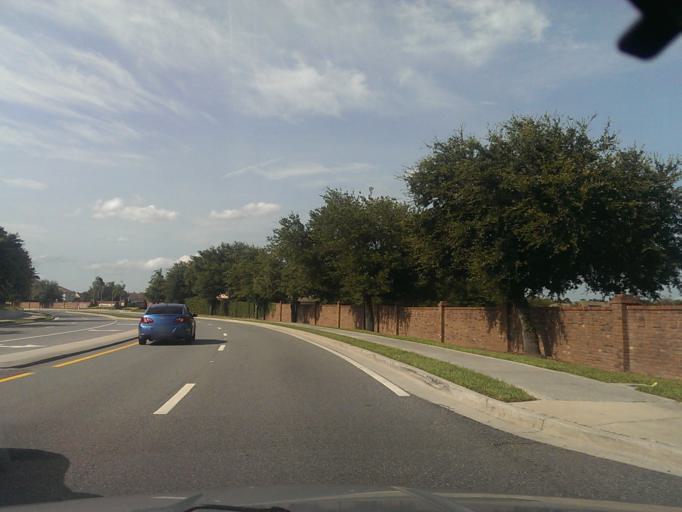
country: US
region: Florida
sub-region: Orange County
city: Lake Butler
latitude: 28.5102
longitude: -81.5843
